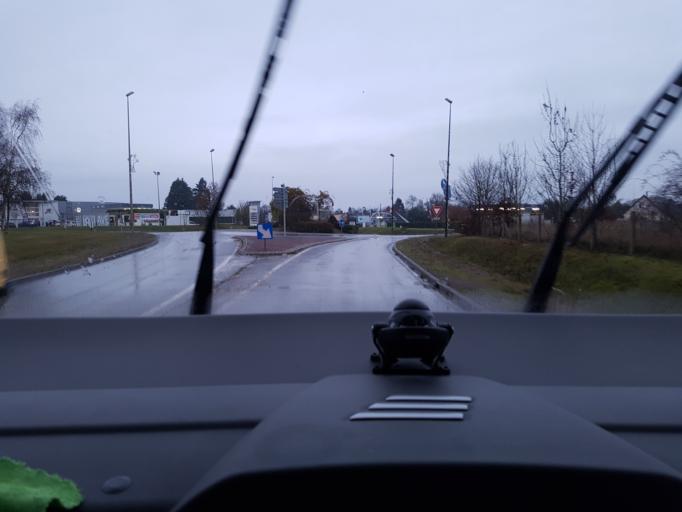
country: FR
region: Haute-Normandie
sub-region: Departement de l'Eure
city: Saint-Pierre-des-Fleurs
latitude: 49.2474
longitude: 0.9625
